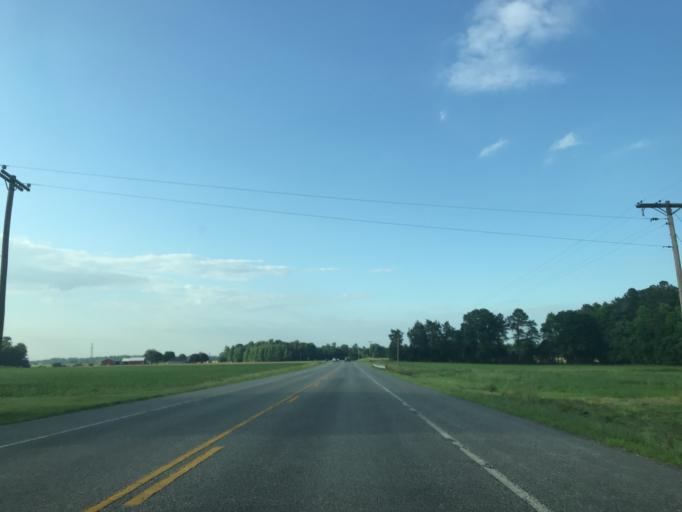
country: US
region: Maryland
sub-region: Caroline County
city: Denton
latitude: 38.8196
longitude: -75.7795
